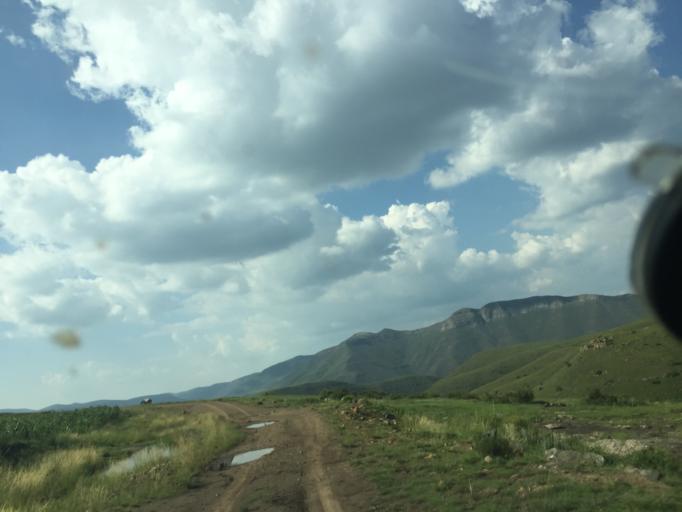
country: LS
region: Maseru
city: Nako
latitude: -29.6297
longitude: 28.1073
